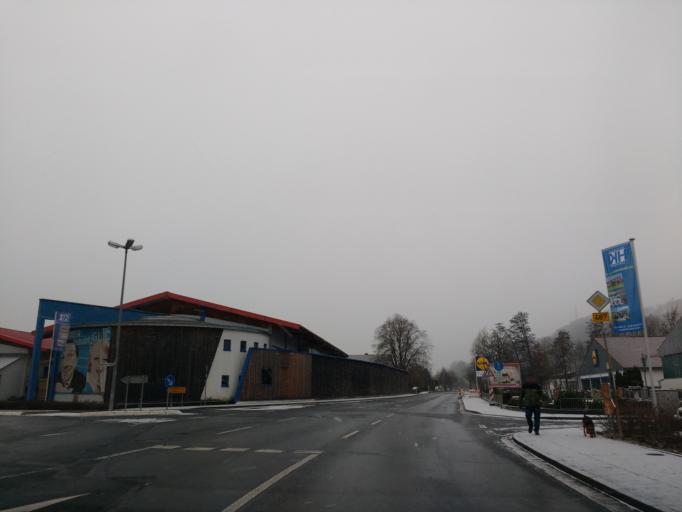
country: DE
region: Hesse
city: Spangenberg
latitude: 51.1153
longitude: 9.6544
